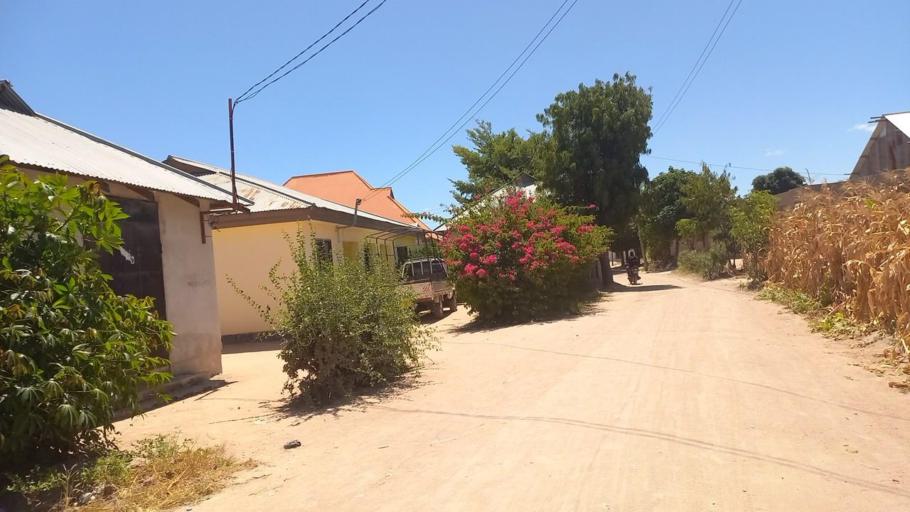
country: TZ
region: Dodoma
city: Dodoma
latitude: -6.1314
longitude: 35.7338
